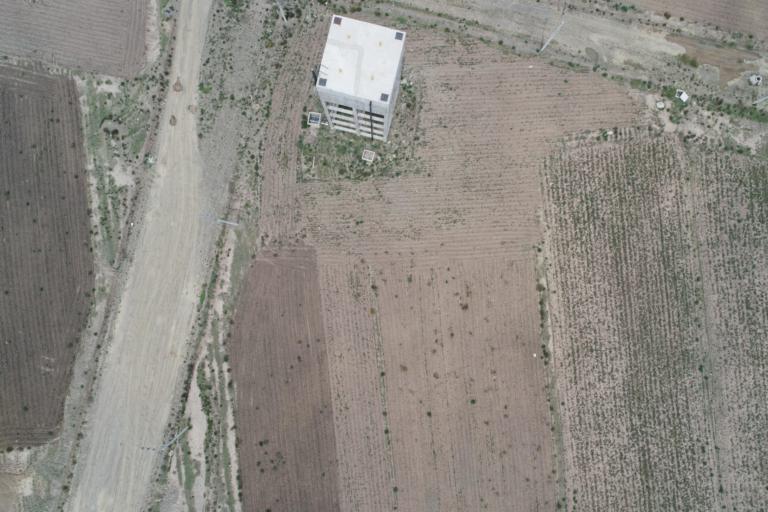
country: BO
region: La Paz
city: La Paz
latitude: -16.5141
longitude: -68.2987
